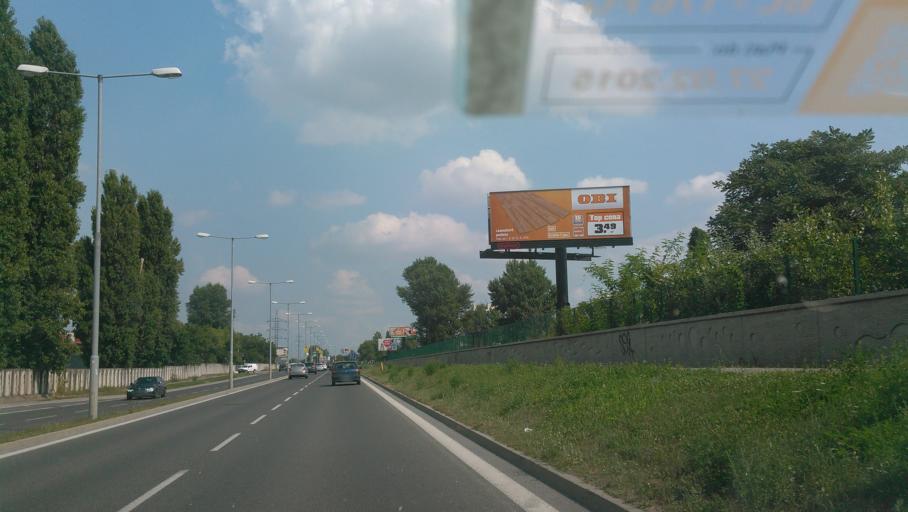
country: SK
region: Bratislavsky
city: Bratislava
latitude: 48.1421
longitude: 17.1362
